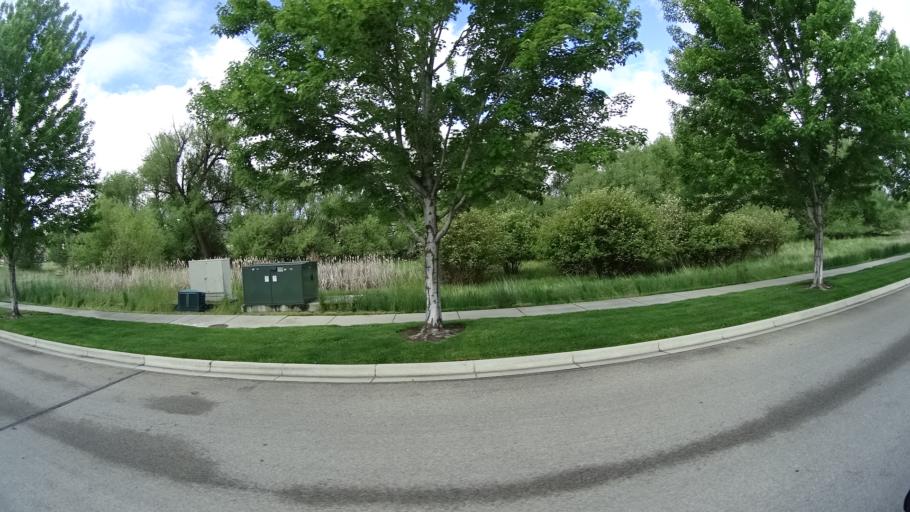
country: US
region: Idaho
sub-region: Ada County
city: Garden City
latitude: 43.7212
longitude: -116.2501
